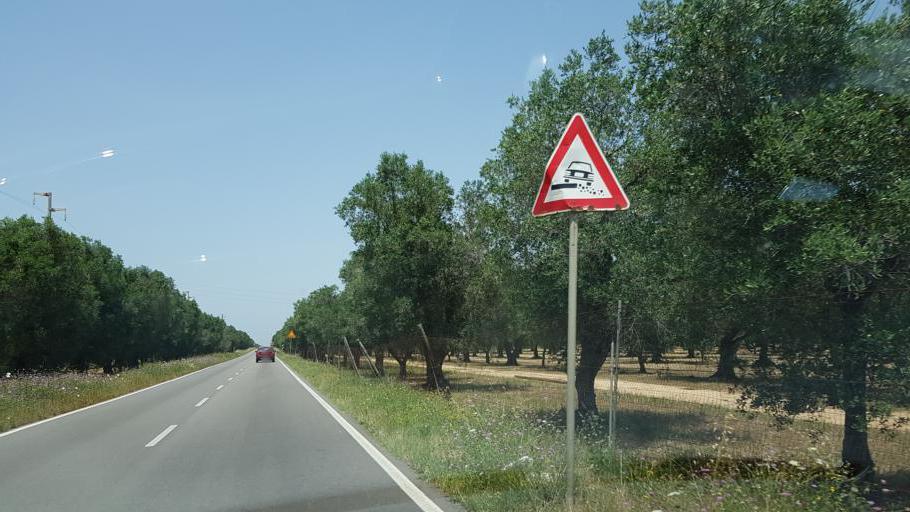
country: IT
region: Apulia
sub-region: Provincia di Brindisi
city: San Pancrazio Salentino
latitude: 40.3582
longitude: 17.8434
